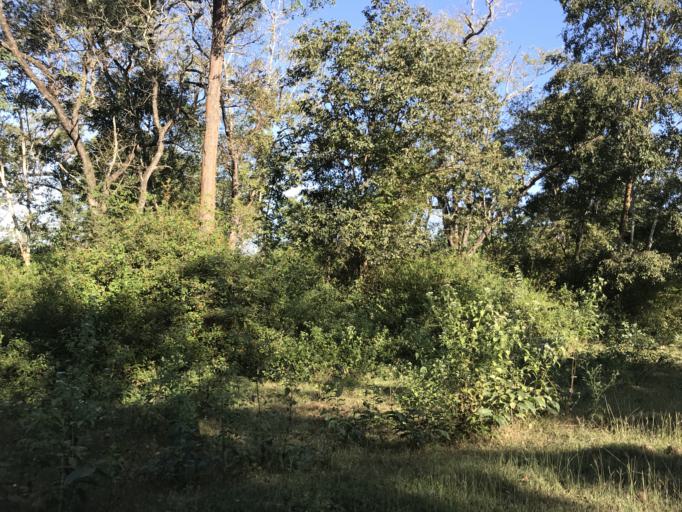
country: IN
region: Karnataka
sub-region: Mysore
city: Heggadadevankote
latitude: 11.9729
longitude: 76.2426
